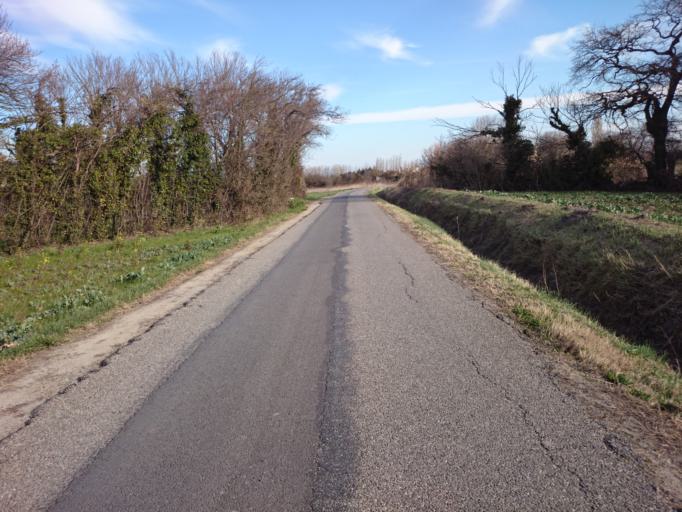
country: FR
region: Provence-Alpes-Cote d'Azur
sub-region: Departement du Vaucluse
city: Saint-Saturnin-les-Avignon
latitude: 43.9704
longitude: 4.9314
